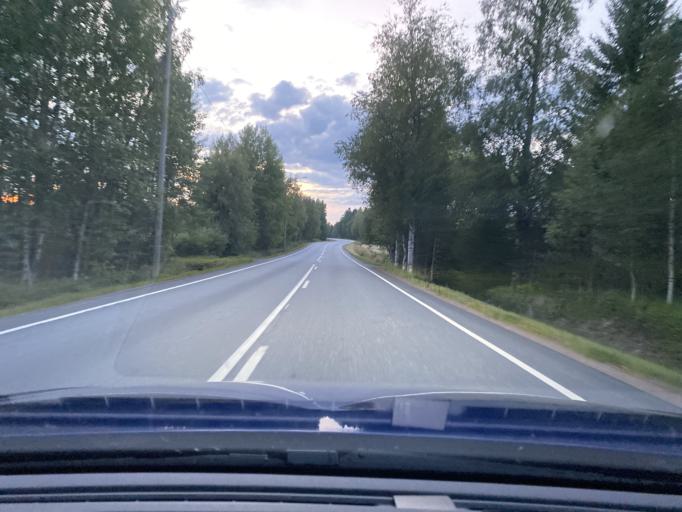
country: FI
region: Satakunta
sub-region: Pohjois-Satakunta
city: Honkajoki
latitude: 62.2168
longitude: 22.2888
